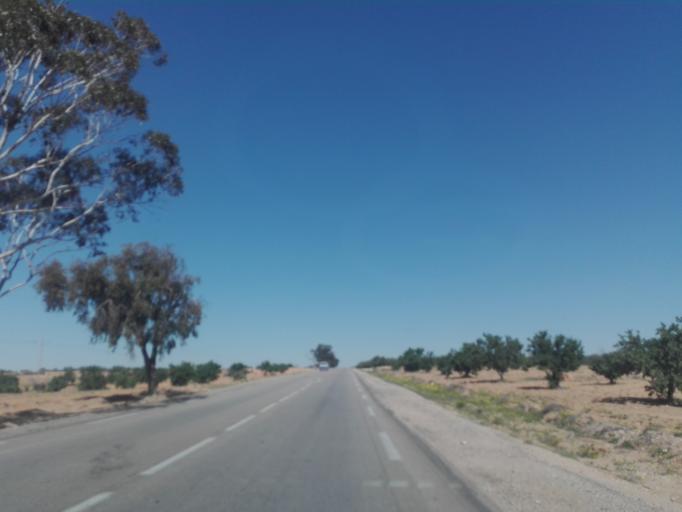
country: TN
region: Safaqis
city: Bi'r `Ali Bin Khalifah
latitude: 34.7479
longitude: 10.3532
